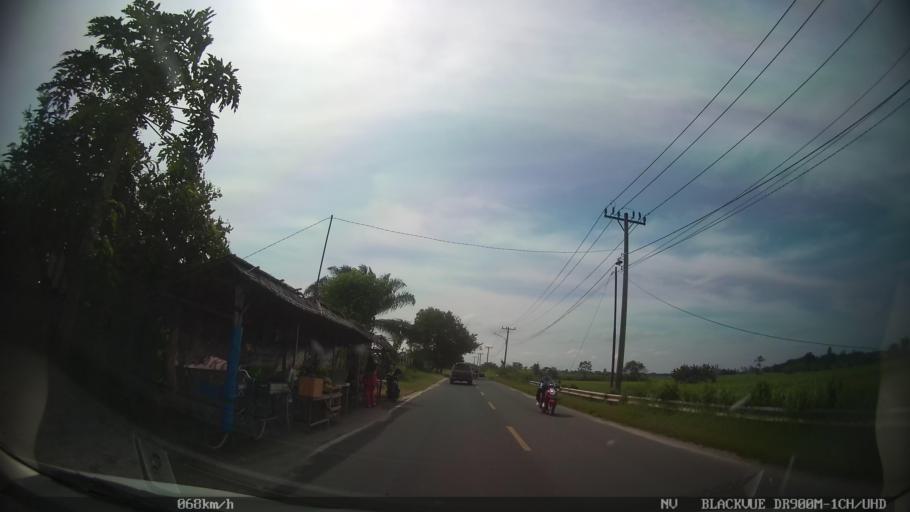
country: ID
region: North Sumatra
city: Percut
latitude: 3.6137
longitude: 98.8434
